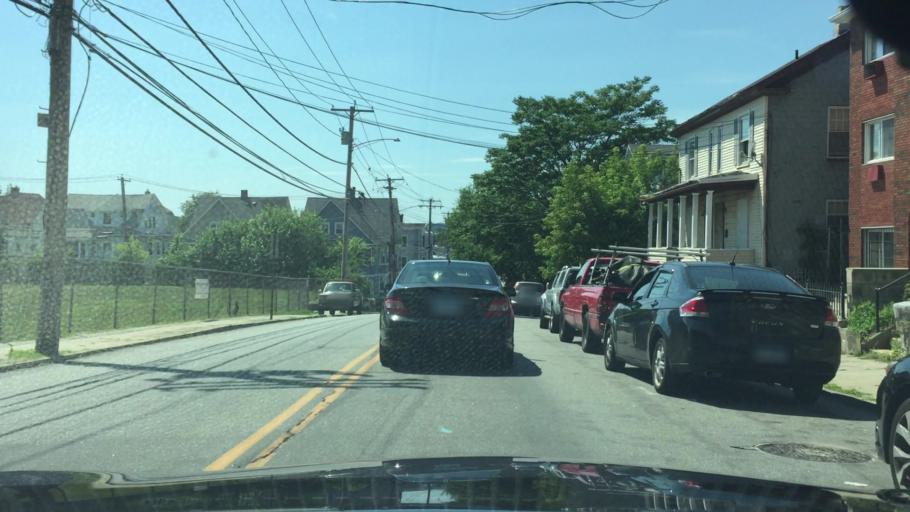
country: US
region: Connecticut
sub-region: Fairfield County
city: Bridgeport
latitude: 41.1807
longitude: -73.1966
